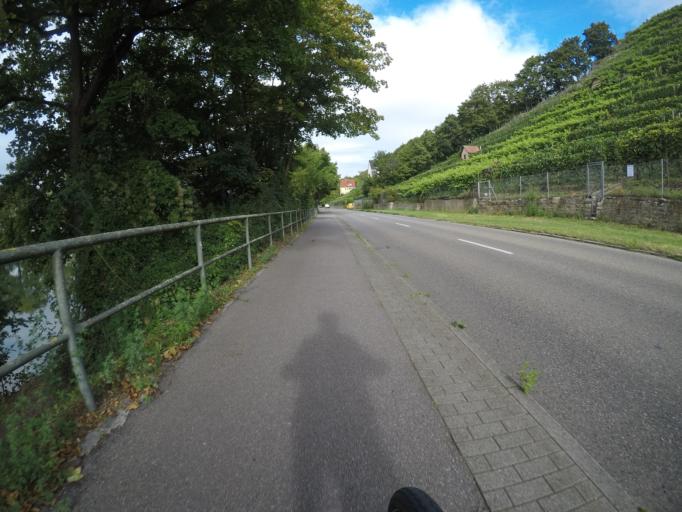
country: DE
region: Baden-Wuerttemberg
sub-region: Regierungsbezirk Stuttgart
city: Stuttgart Muehlhausen
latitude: 48.8255
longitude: 9.2219
